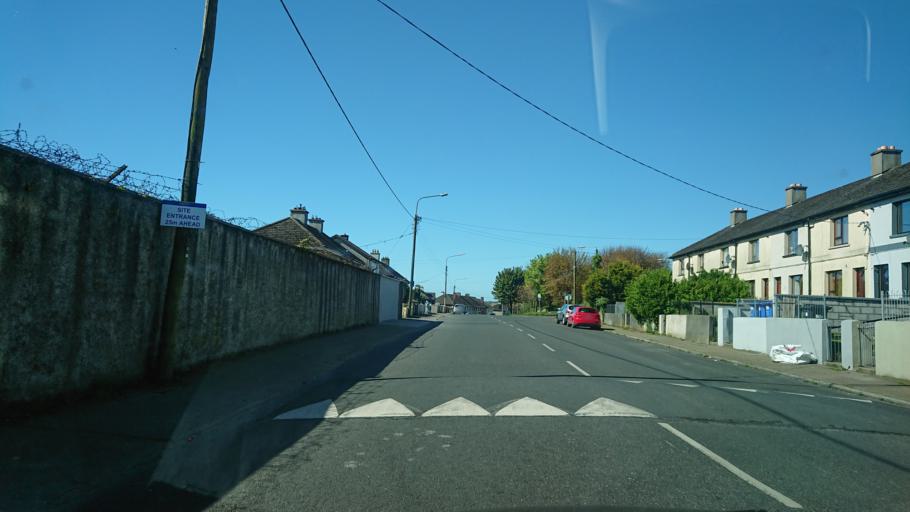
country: IE
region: Munster
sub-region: Waterford
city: Waterford
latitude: 52.2527
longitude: -7.1212
